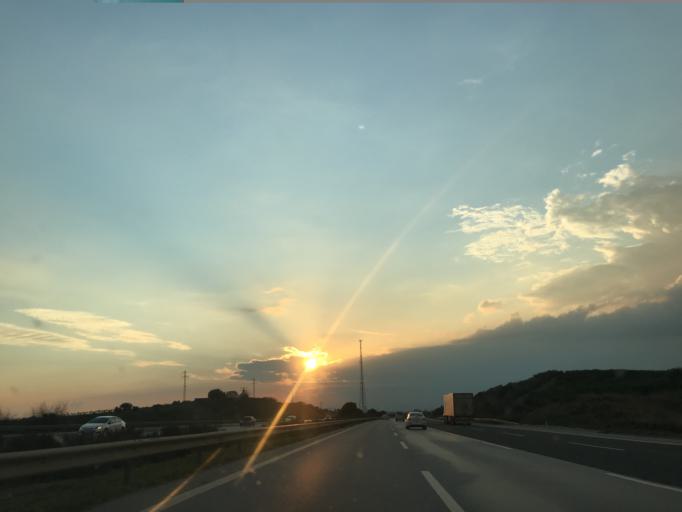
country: TR
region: Mersin
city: Yenice
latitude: 37.0235
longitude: 35.0960
